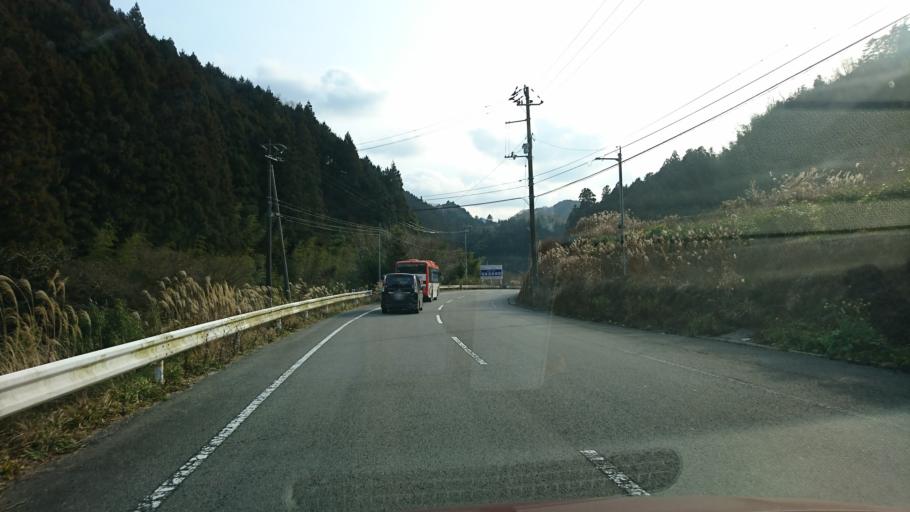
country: JP
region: Ehime
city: Hojo
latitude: 33.9216
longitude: 132.8863
